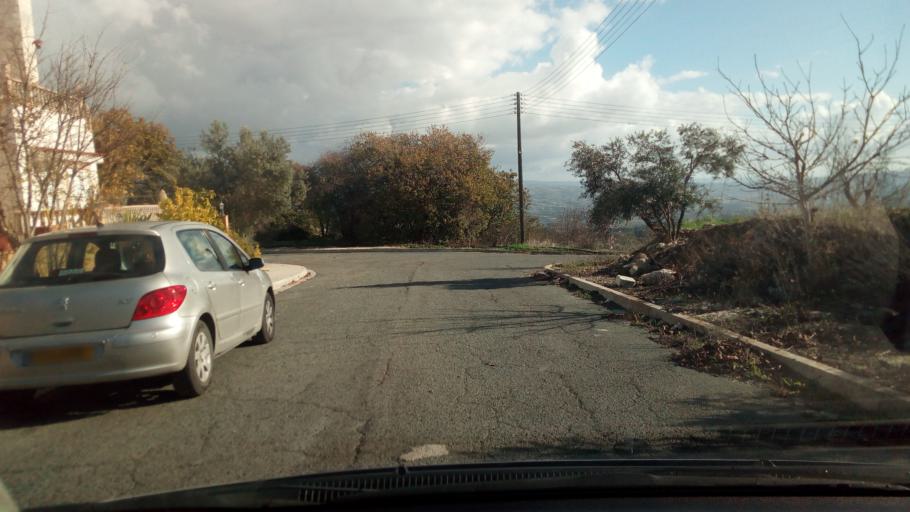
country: CY
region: Pafos
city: Mesogi
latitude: 34.8842
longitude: 32.5119
